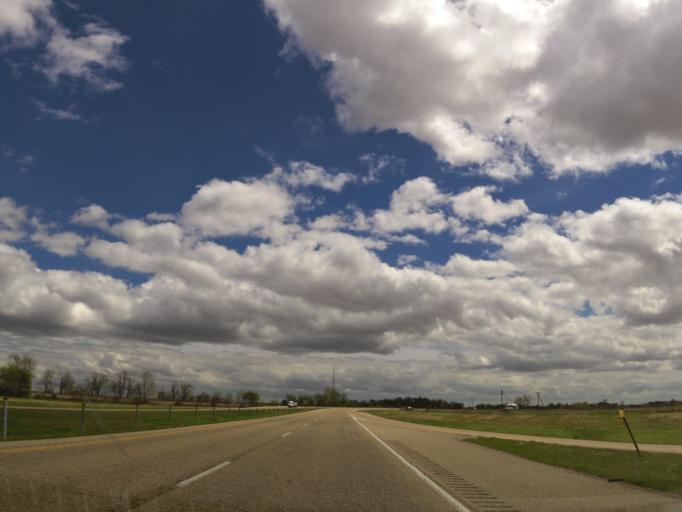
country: US
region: Arkansas
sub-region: Poinsett County
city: Marked Tree
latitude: 35.4717
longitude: -90.3317
